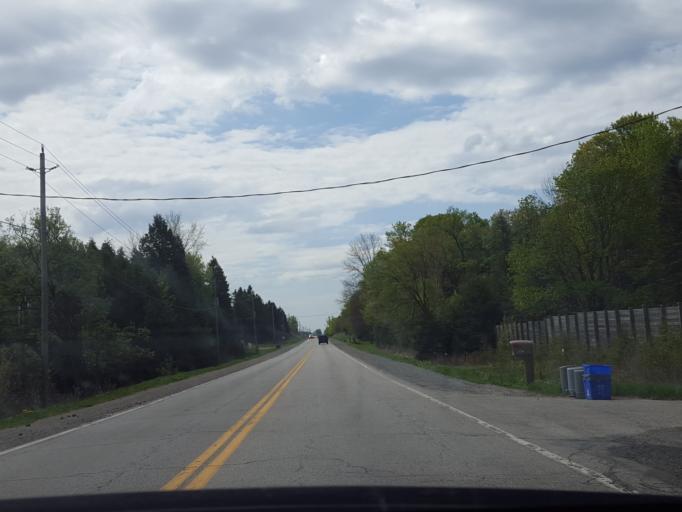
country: CA
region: Ontario
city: Oshawa
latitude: 43.9476
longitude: -78.7184
